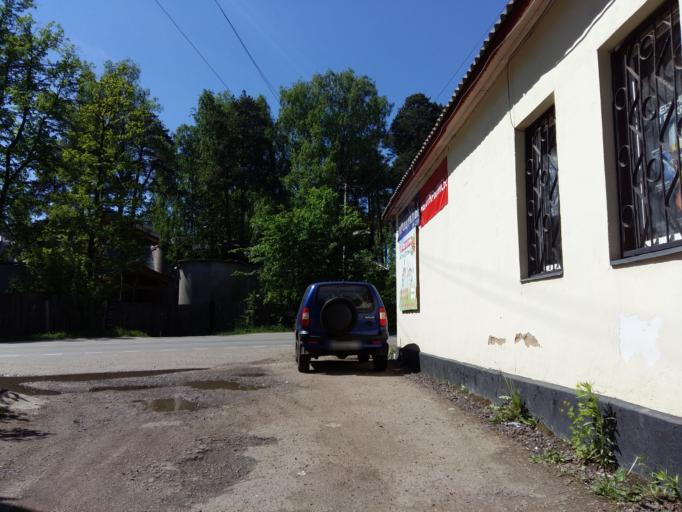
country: RU
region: Moskovskaya
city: Mamontovka
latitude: 55.9694
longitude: 37.8289
